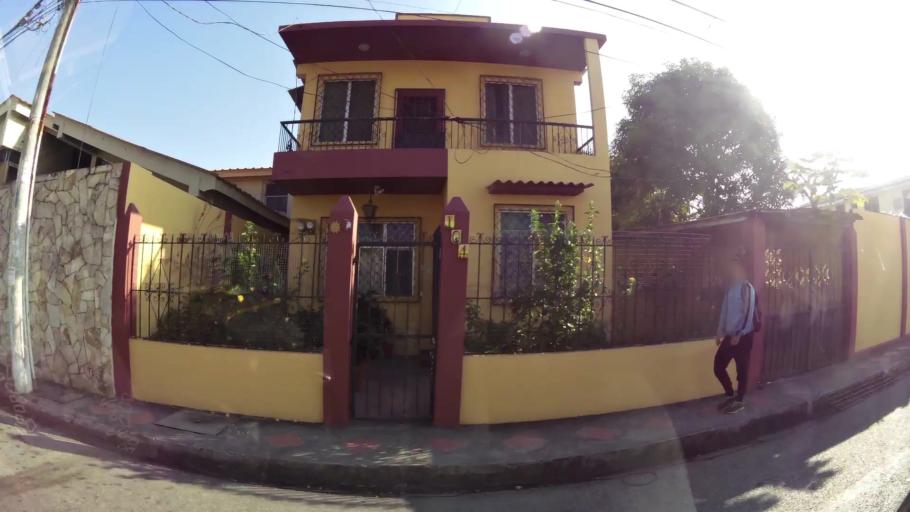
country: EC
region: Guayas
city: Guayaquil
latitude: -2.1597
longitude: -79.9056
